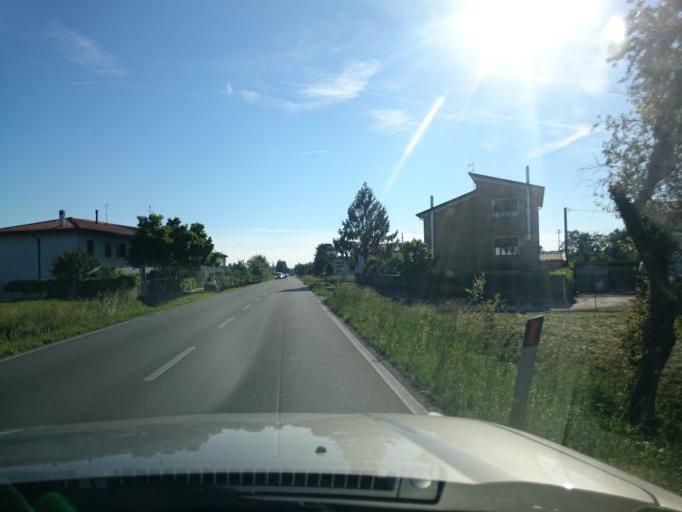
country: IT
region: Veneto
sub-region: Provincia di Venezia
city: Noale
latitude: 45.5392
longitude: 12.0629
